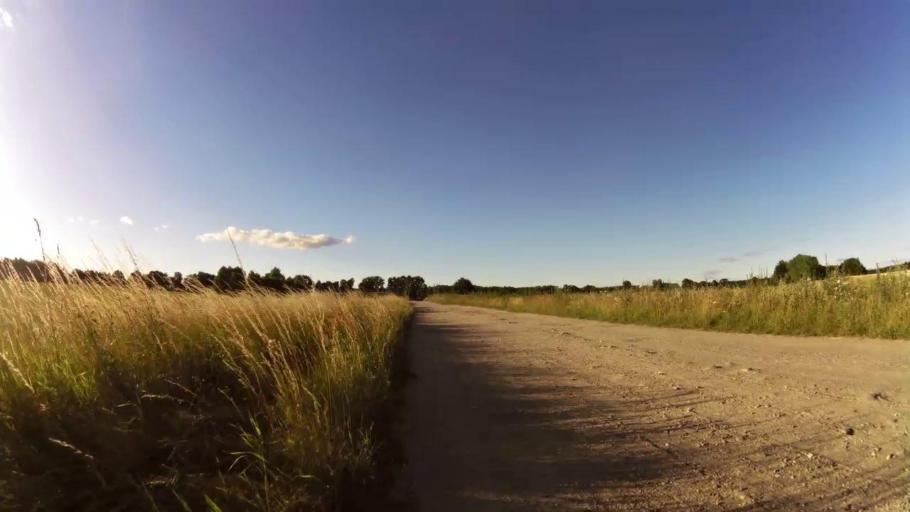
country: PL
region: West Pomeranian Voivodeship
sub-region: Powiat swidwinski
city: Swidwin
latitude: 53.7413
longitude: 15.8603
